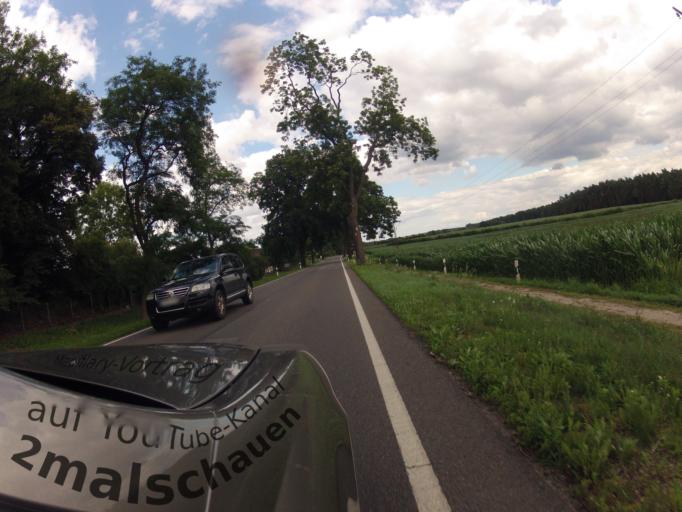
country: DE
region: Mecklenburg-Vorpommern
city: Anklam
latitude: 53.9040
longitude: 13.7654
